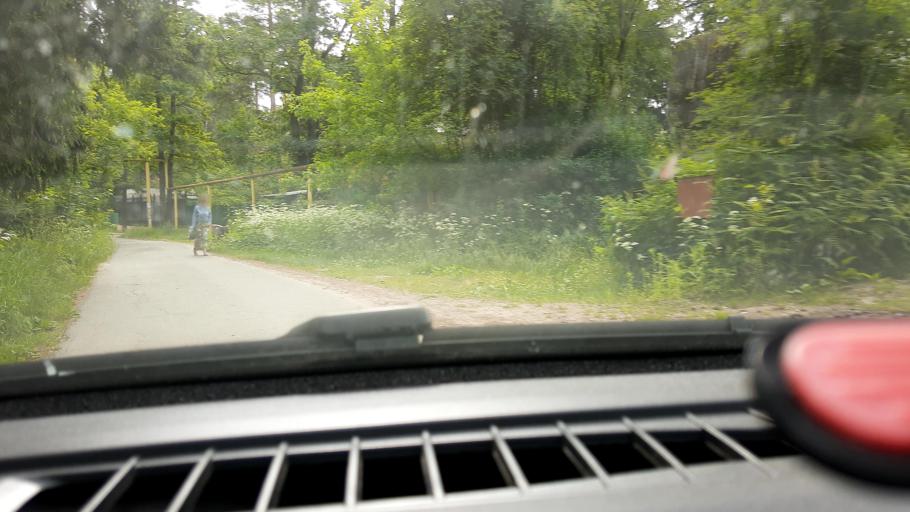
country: RU
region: Nizjnij Novgorod
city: Afonino
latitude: 56.1861
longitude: 44.1065
